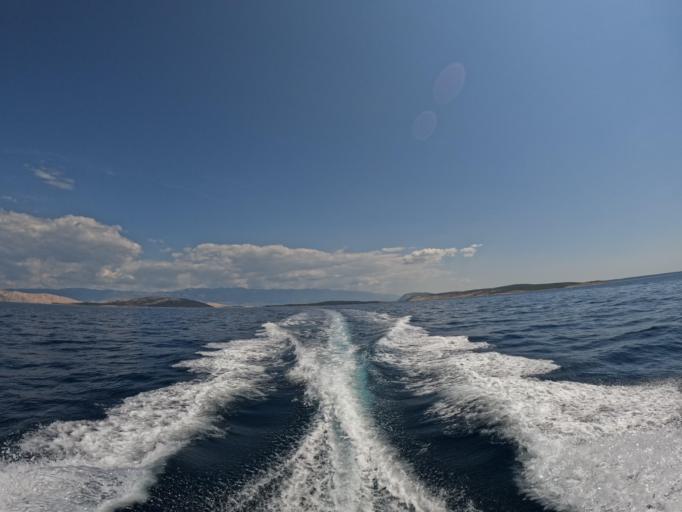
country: HR
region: Primorsko-Goranska
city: Lopar
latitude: 44.8696
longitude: 14.6755
